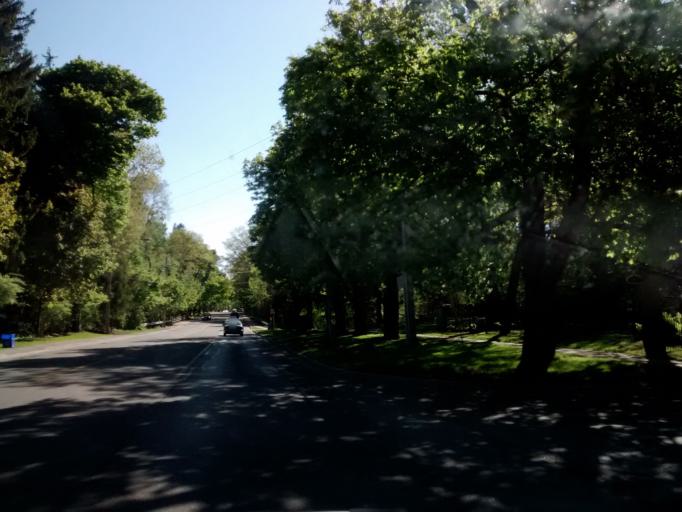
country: CA
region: Ontario
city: Burlington
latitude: 43.3626
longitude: -79.7413
